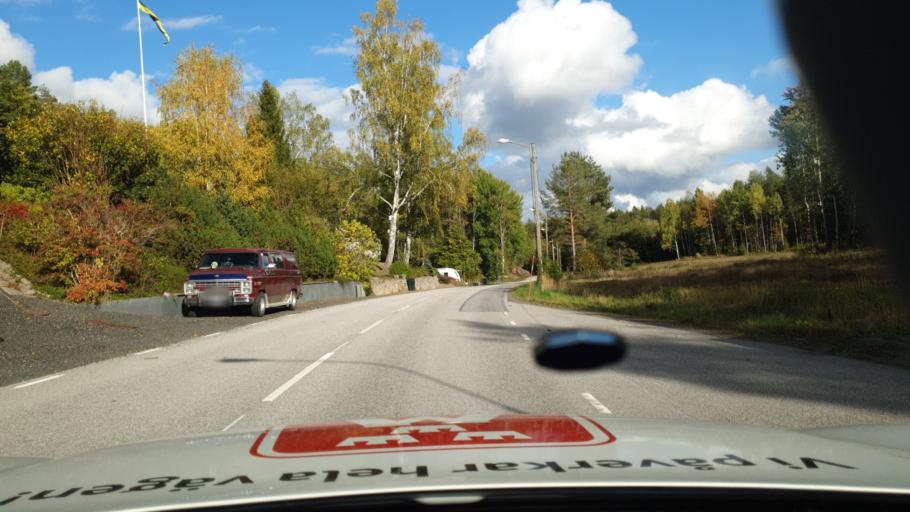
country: SE
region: OEstergoetland
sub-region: Valdemarsviks Kommun
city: Valdemarsvik
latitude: 58.1450
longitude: 16.5156
